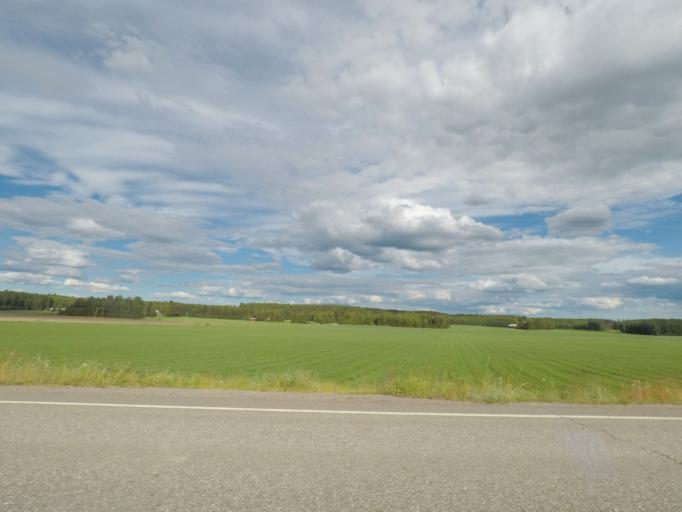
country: FI
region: Paijanne Tavastia
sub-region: Lahti
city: Hollola
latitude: 60.8560
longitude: 25.4990
